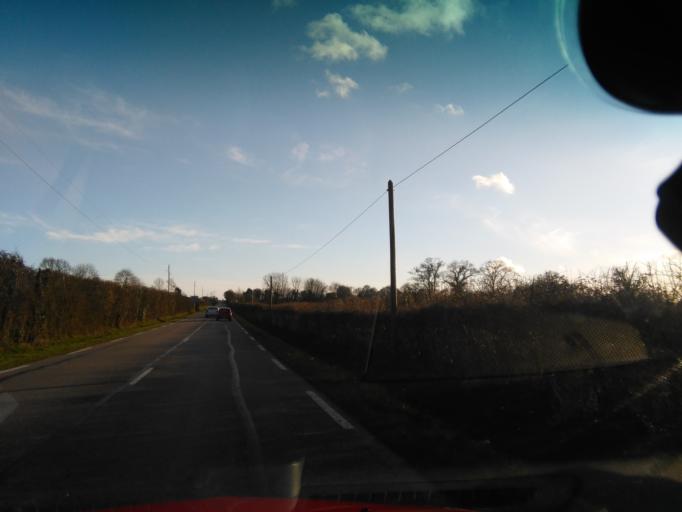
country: FR
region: Lower Normandy
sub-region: Departement de l'Orne
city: Pont-Ecrepin
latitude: 48.7992
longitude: -0.2439
